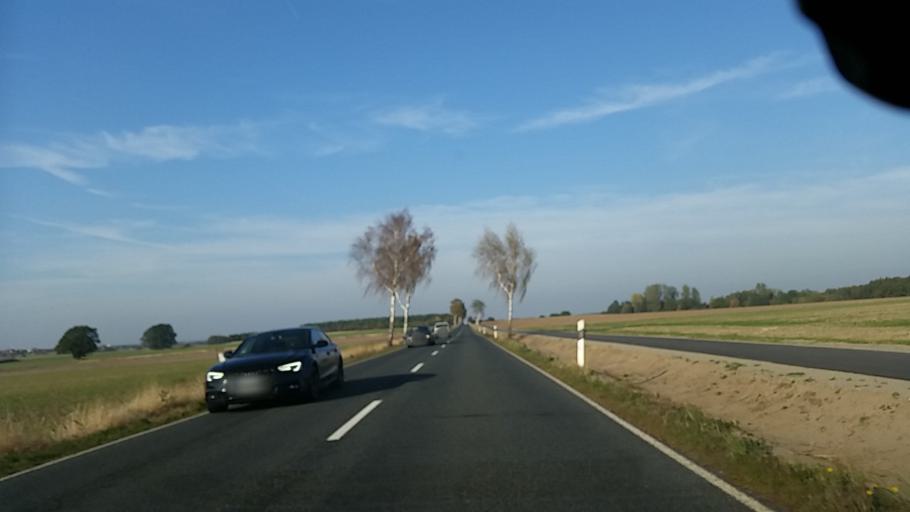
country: DE
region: Lower Saxony
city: Gross Twulpstedt
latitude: 52.3746
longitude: 10.8495
